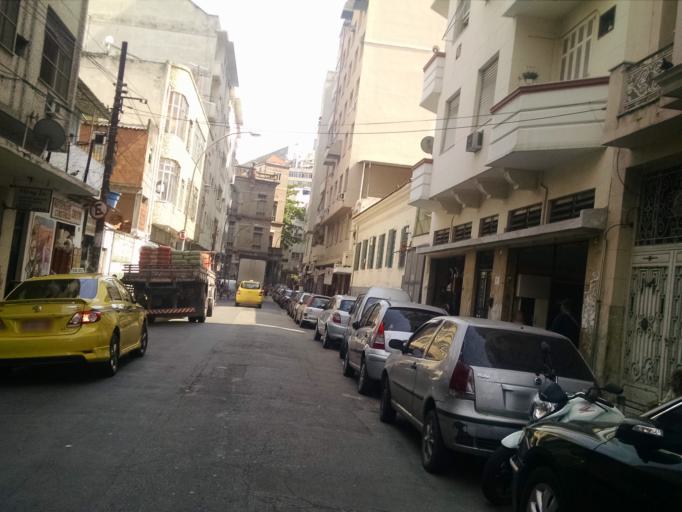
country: BR
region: Rio de Janeiro
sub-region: Rio De Janeiro
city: Rio de Janeiro
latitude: -22.9146
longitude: -43.1869
